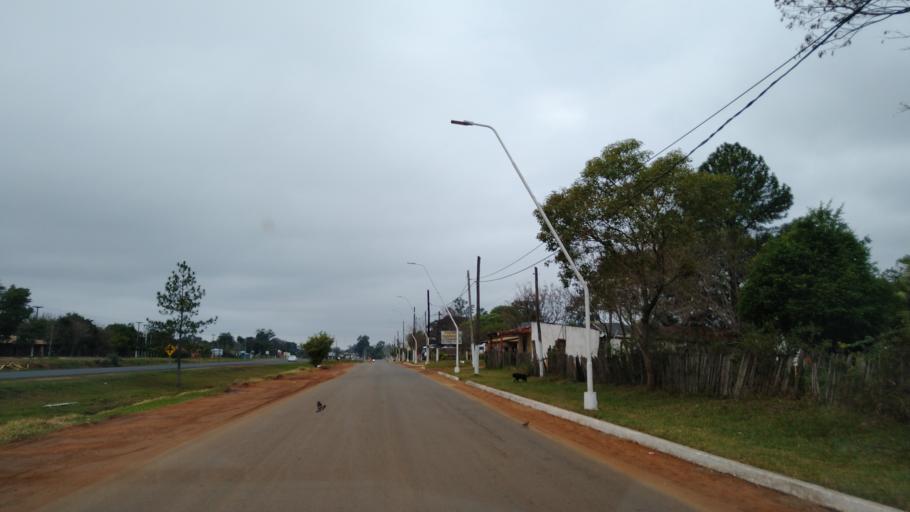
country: AR
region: Corrientes
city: Alvear
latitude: -29.0861
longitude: -56.5587
